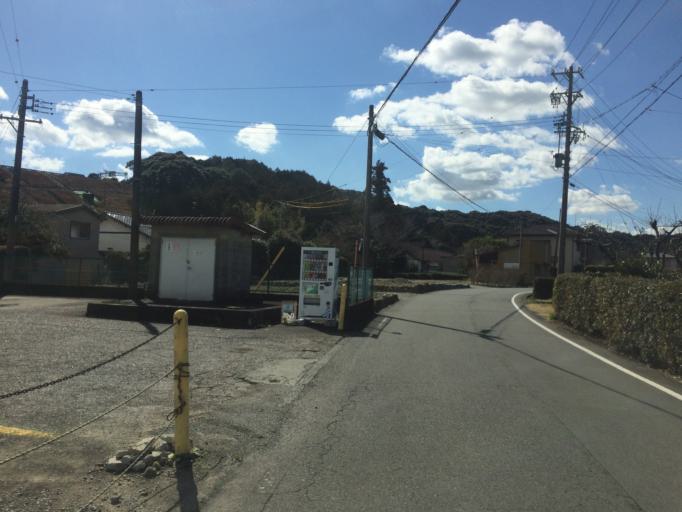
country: JP
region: Shizuoka
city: Shimada
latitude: 34.7577
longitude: 138.1921
